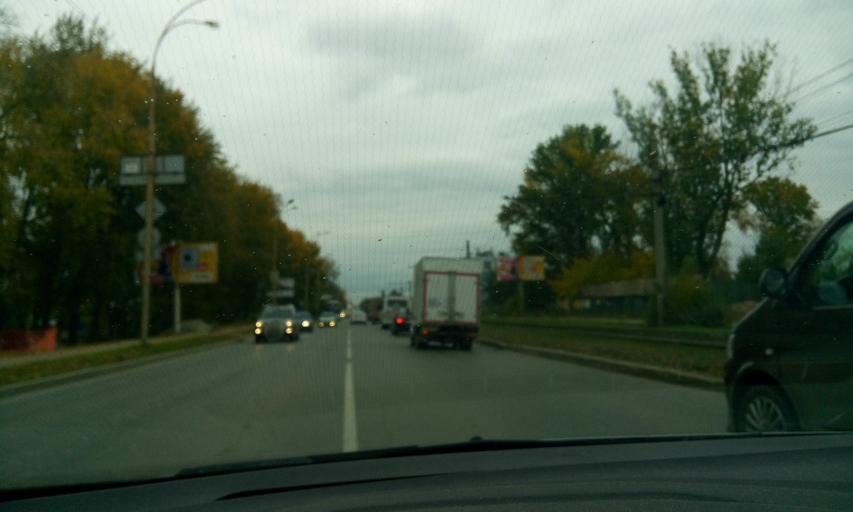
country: RU
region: Sverdlovsk
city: Yekaterinburg
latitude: 56.8609
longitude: 60.6611
